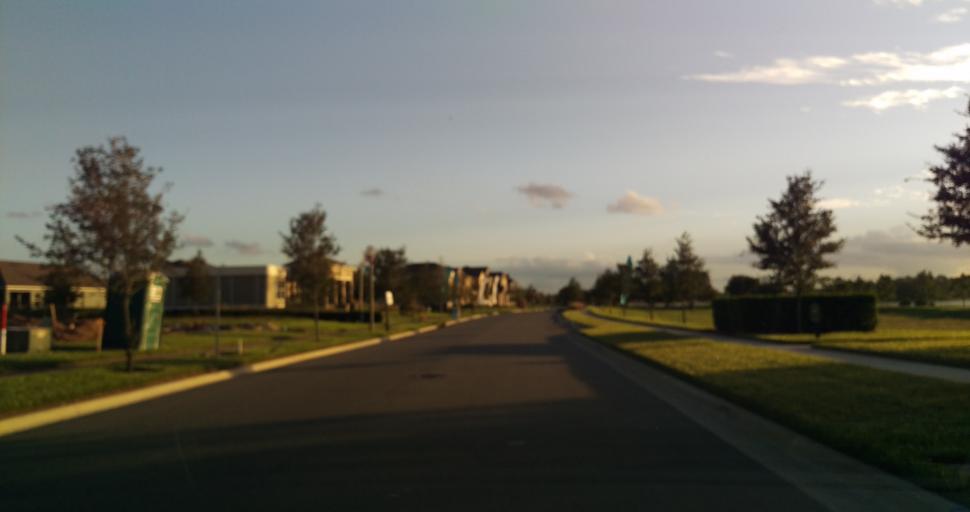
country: US
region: Florida
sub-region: Polk County
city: Citrus Ridge
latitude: 28.4293
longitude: -81.6371
